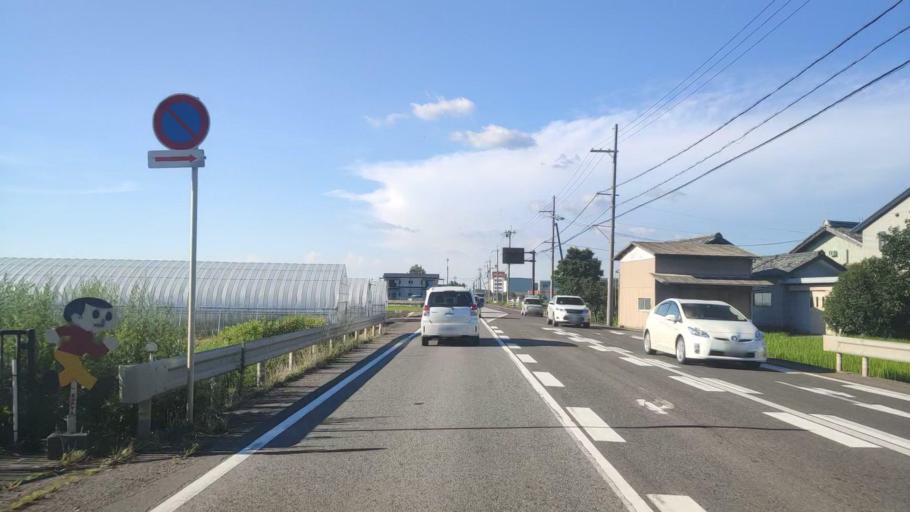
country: JP
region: Shiga Prefecture
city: Youkaichi
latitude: 35.0783
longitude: 136.2491
